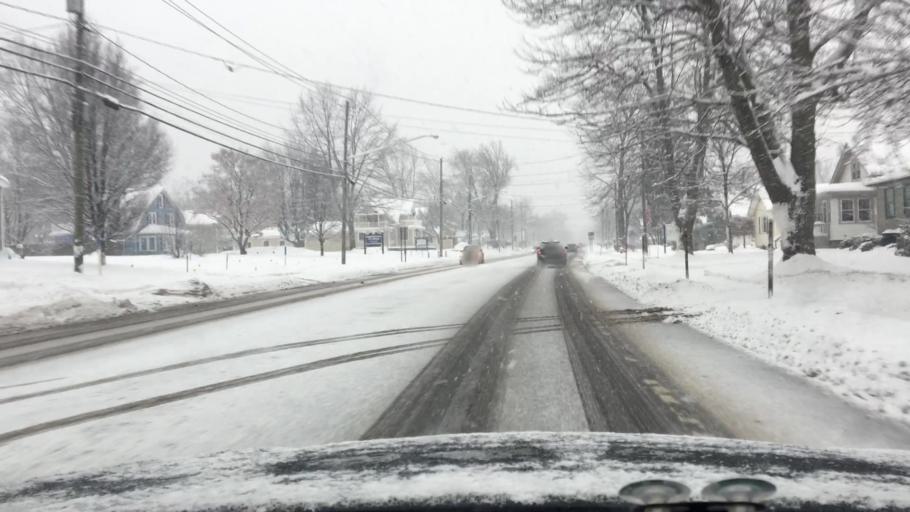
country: US
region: New York
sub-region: Erie County
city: Orchard Park
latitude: 42.7796
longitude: -78.7455
